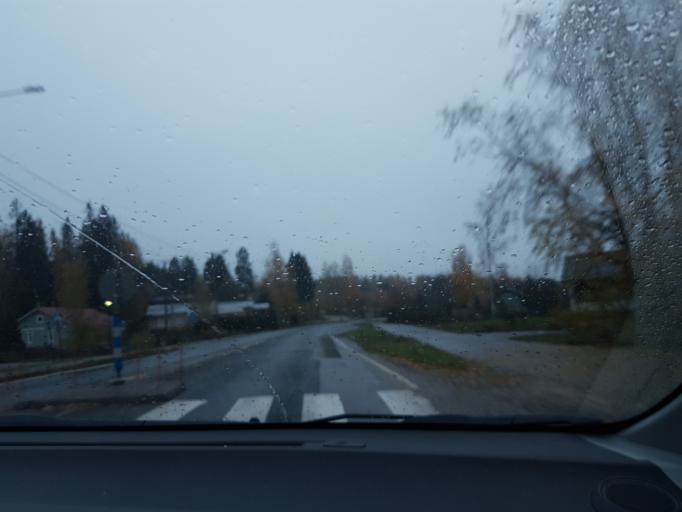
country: FI
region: Uusimaa
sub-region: Helsinki
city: Jaervenpaeae
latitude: 60.5405
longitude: 25.1144
